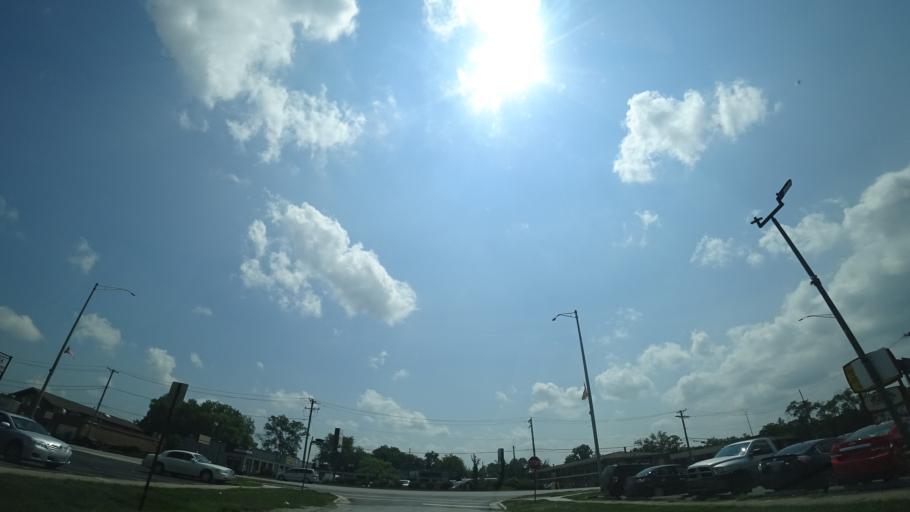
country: US
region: Illinois
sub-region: Cook County
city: Chicago Ridge
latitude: 41.6908
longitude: -87.7812
